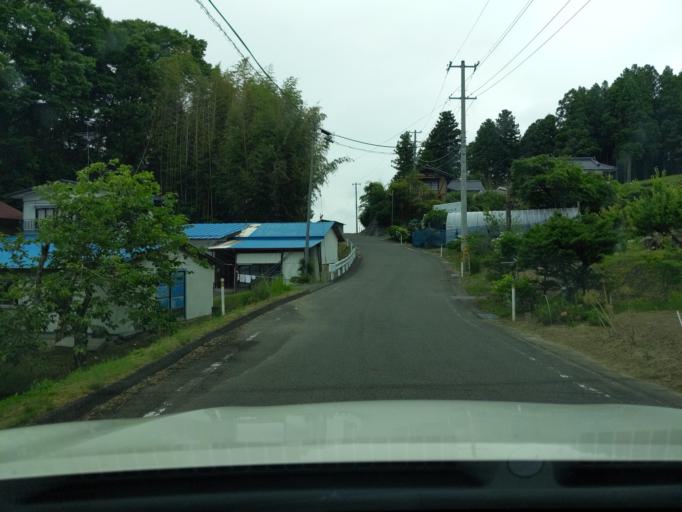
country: JP
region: Fukushima
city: Miharu
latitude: 37.4145
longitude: 140.4420
